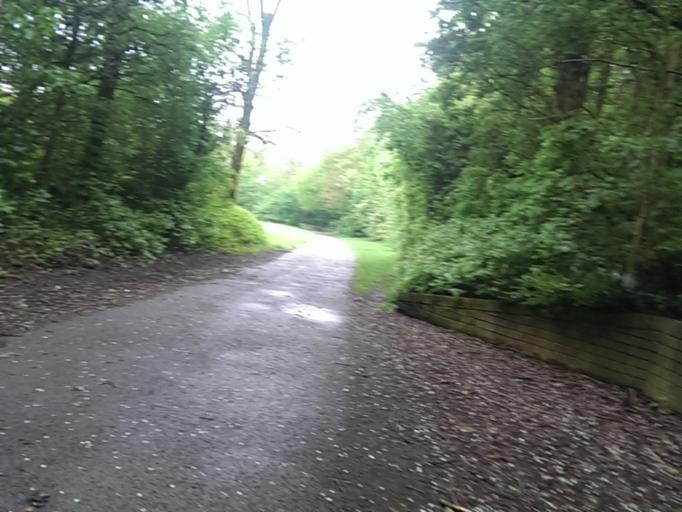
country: GB
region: England
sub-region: Warrington
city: Culcheth
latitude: 53.4253
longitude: -2.5141
